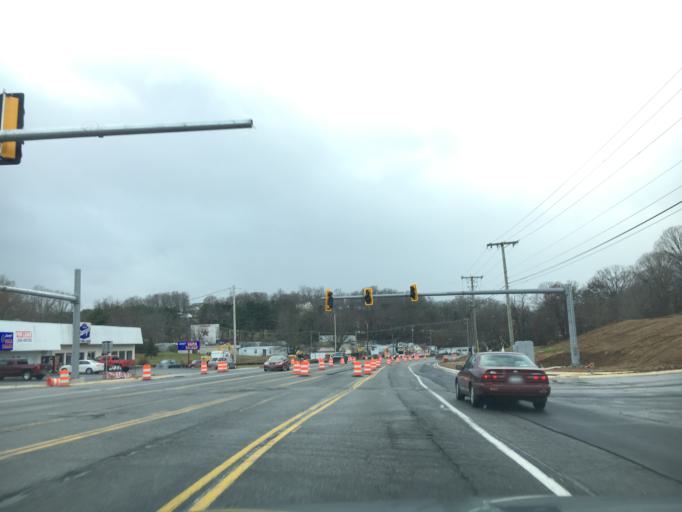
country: US
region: Virginia
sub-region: Montgomery County
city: Christiansburg
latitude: 37.1330
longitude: -80.3773
